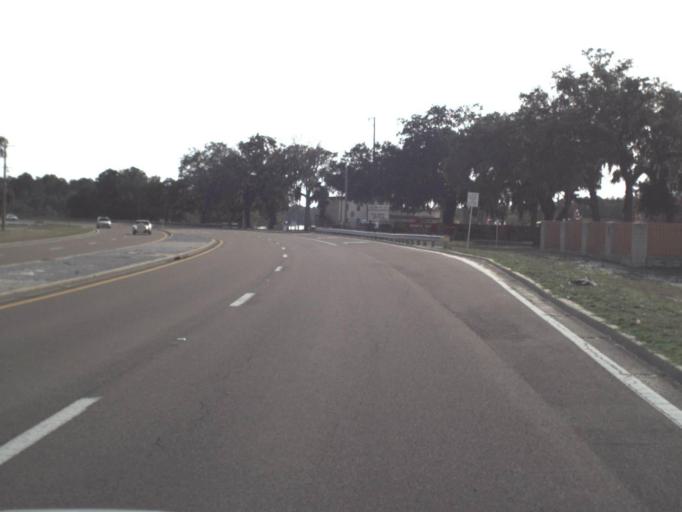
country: US
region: Florida
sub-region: Bay County
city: Tyndall Air Force Base
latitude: 30.1005
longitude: -85.6118
